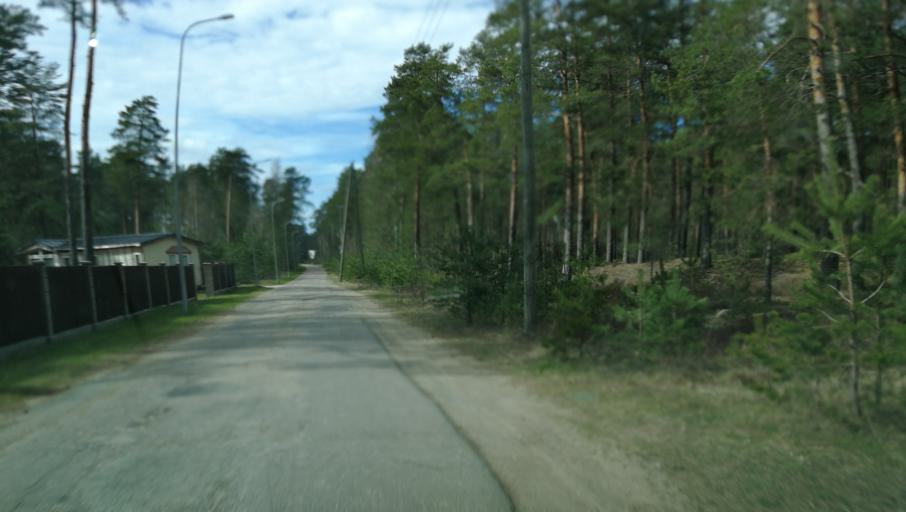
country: LV
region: Garkalne
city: Garkalne
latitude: 57.0386
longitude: 24.4404
